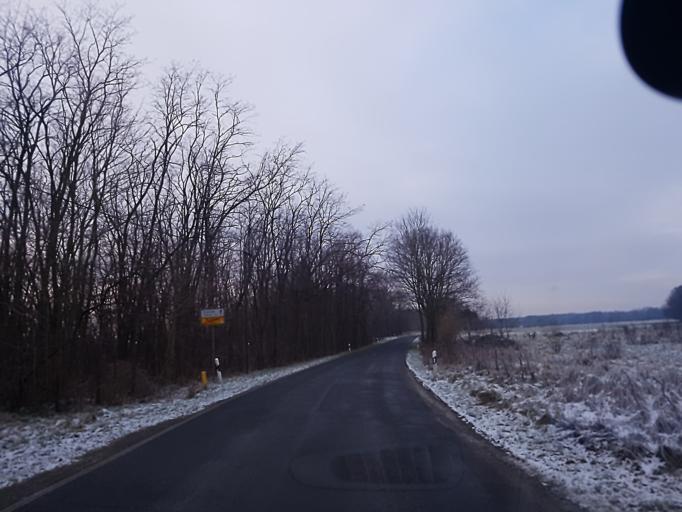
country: DE
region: Brandenburg
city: Lubbenau
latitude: 51.8264
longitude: 13.9188
